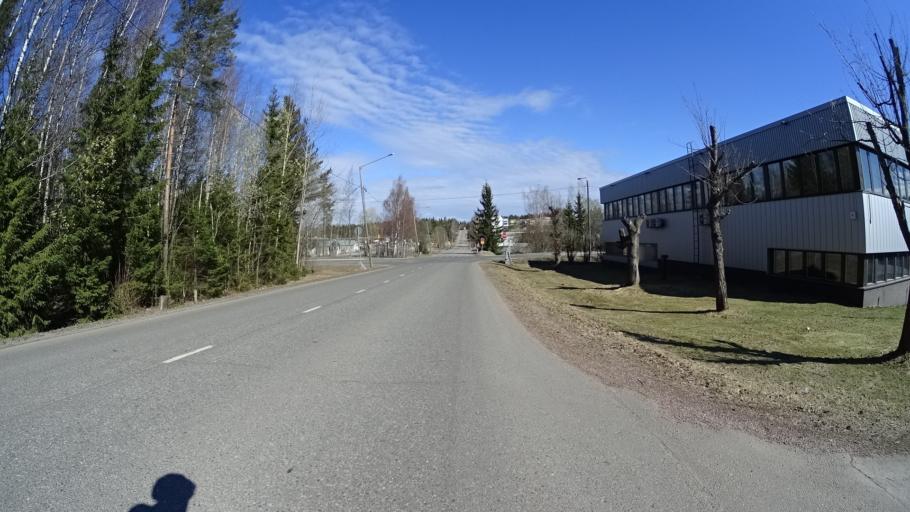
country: FI
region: Uusimaa
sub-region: Helsinki
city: Kilo
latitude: 60.2783
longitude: 24.7582
